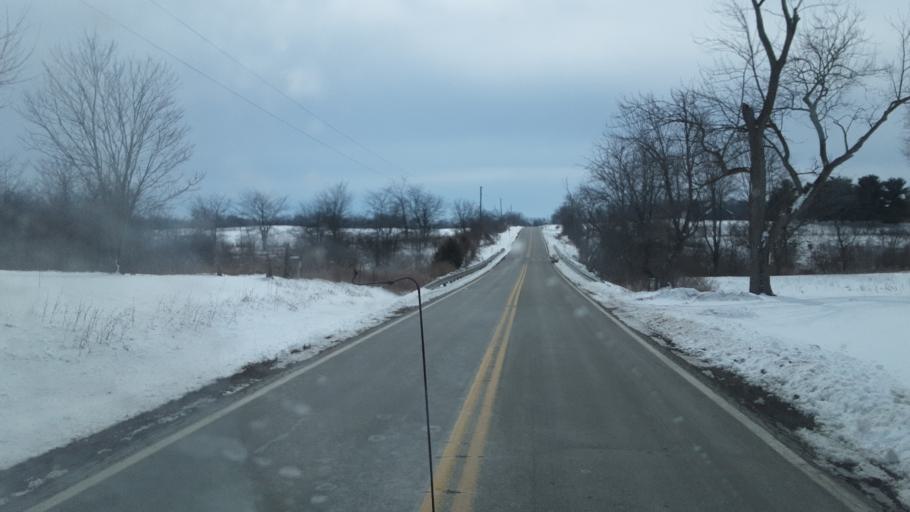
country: US
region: Ohio
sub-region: Madison County
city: Choctaw Lake
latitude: 39.9998
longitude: -83.4986
